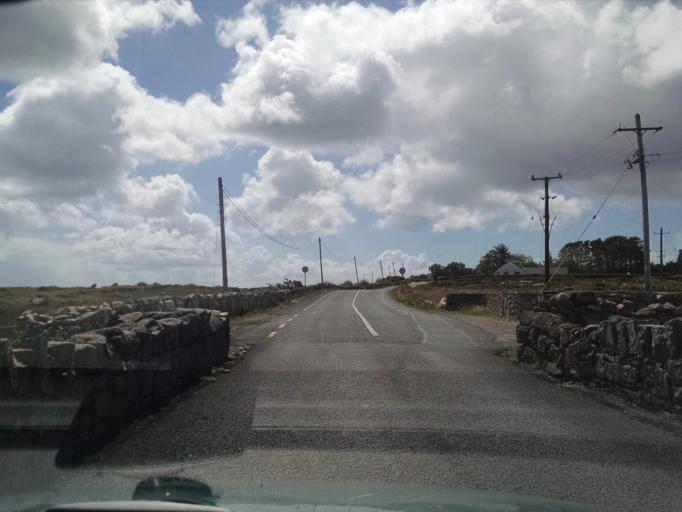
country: IE
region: Connaught
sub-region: County Galway
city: Oughterard
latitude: 53.2837
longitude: -9.6557
